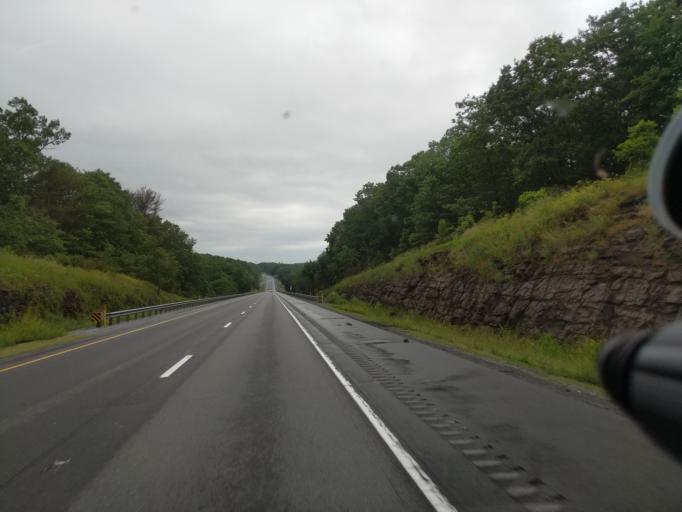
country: US
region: Pennsylvania
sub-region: Lycoming County
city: Jersey Shore
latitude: 41.0649
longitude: -77.2220
